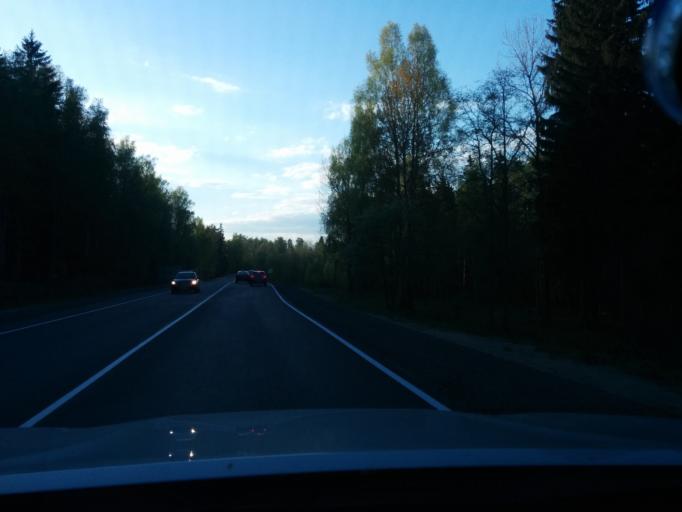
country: RU
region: Leningrad
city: Verkhniye Osel'ki
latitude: 60.2263
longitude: 30.4339
